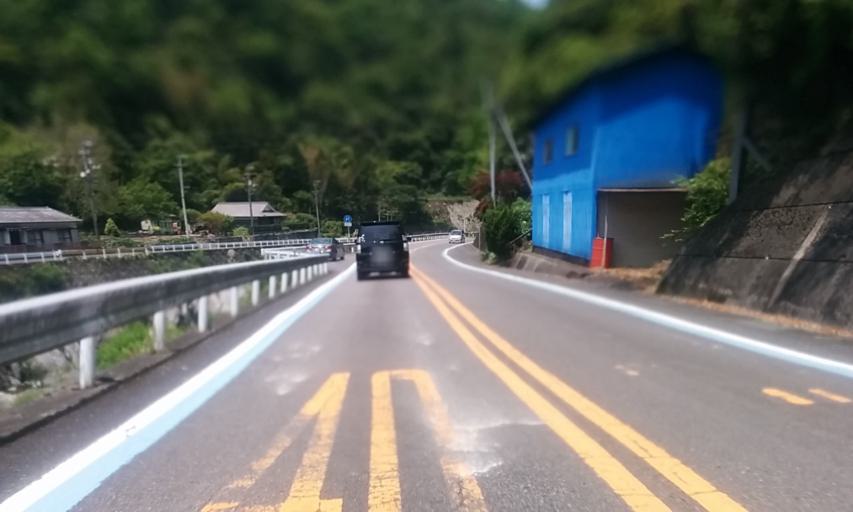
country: JP
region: Ehime
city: Niihama
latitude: 33.9142
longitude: 133.3117
